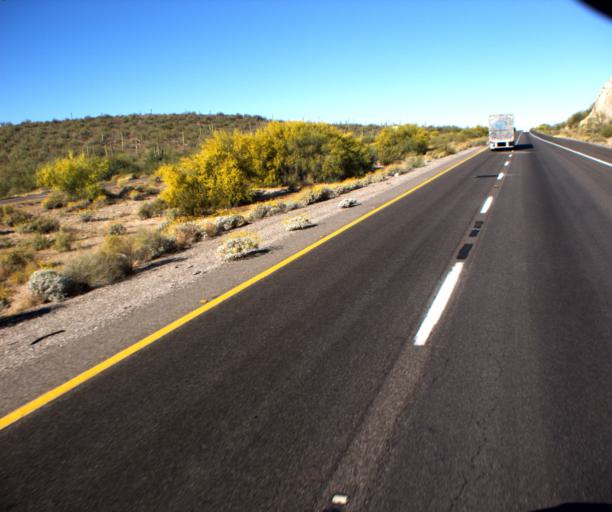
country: US
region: Arizona
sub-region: Pinal County
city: Maricopa
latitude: 32.8351
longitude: -112.1507
